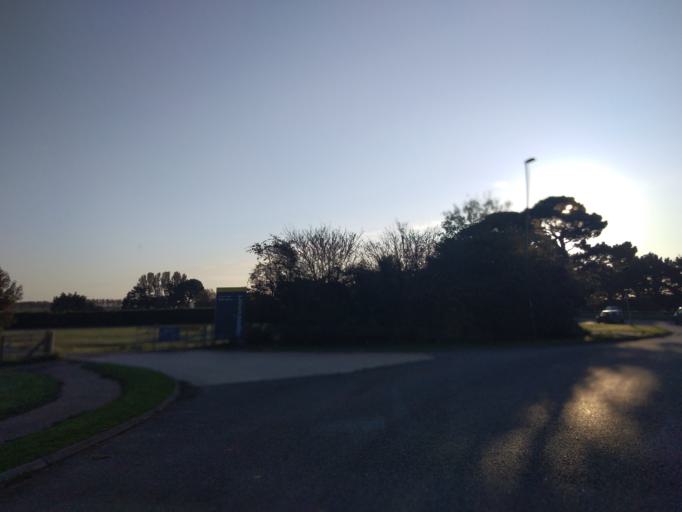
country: GB
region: England
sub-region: West Sussex
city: Rustington
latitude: 50.8186
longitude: -0.4689
